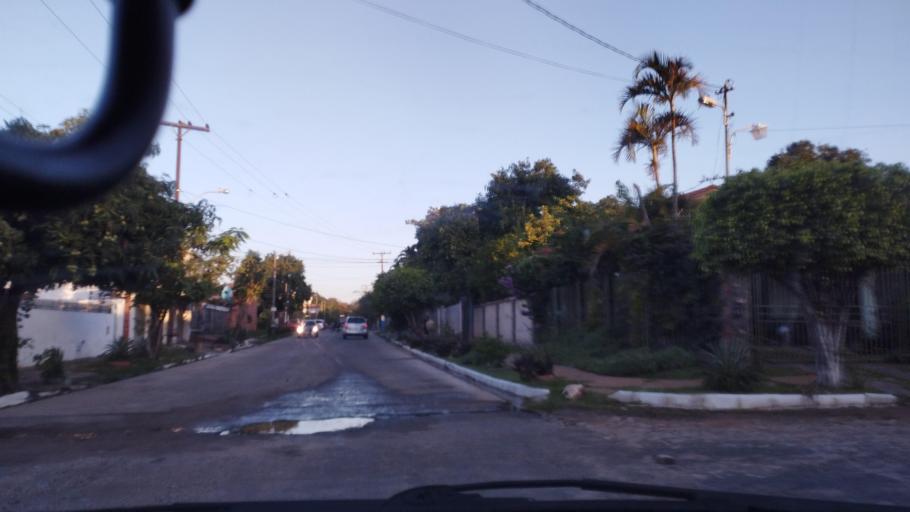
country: PY
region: Central
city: Fernando de la Mora
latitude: -25.2982
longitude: -57.5427
